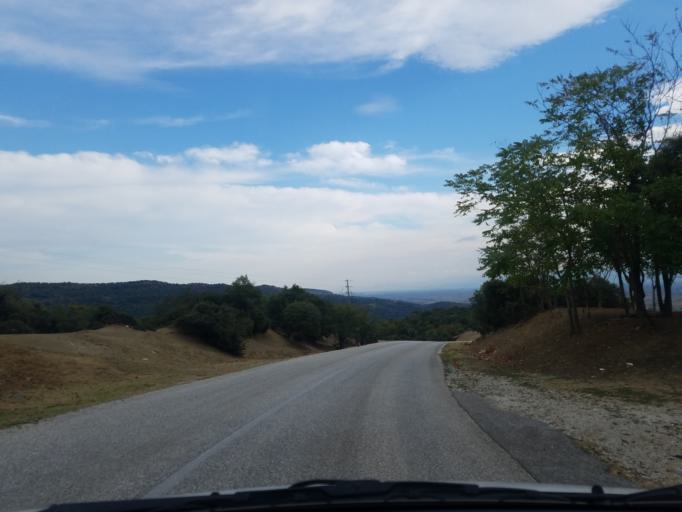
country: GR
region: Thessaly
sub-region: Trikala
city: Kalampaka
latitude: 39.7122
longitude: 21.6529
